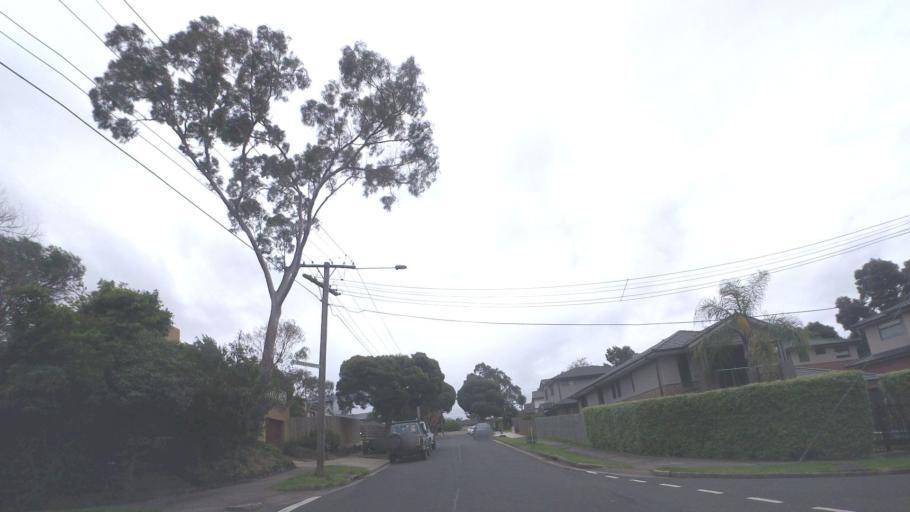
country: AU
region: Victoria
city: Mitcham
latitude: -37.8069
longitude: 145.1979
